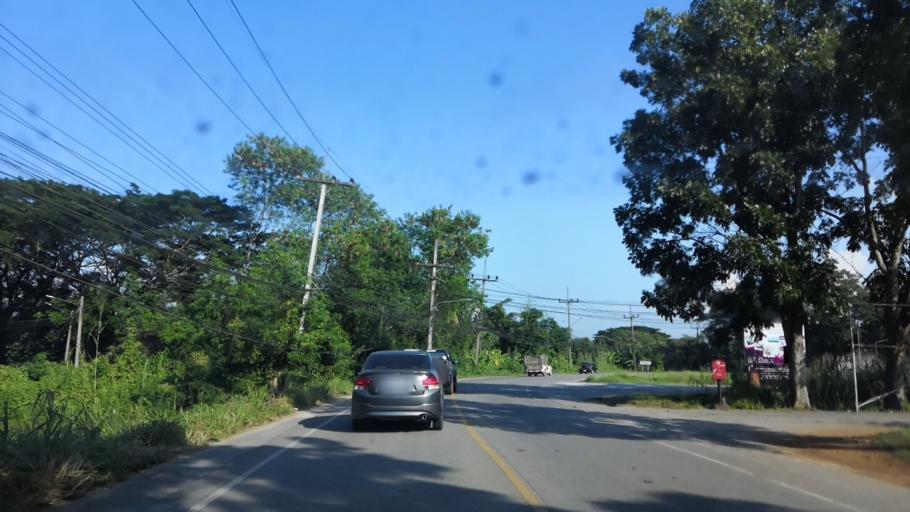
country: TH
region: Chiang Rai
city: Chiang Rai
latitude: 19.9311
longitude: 99.8663
